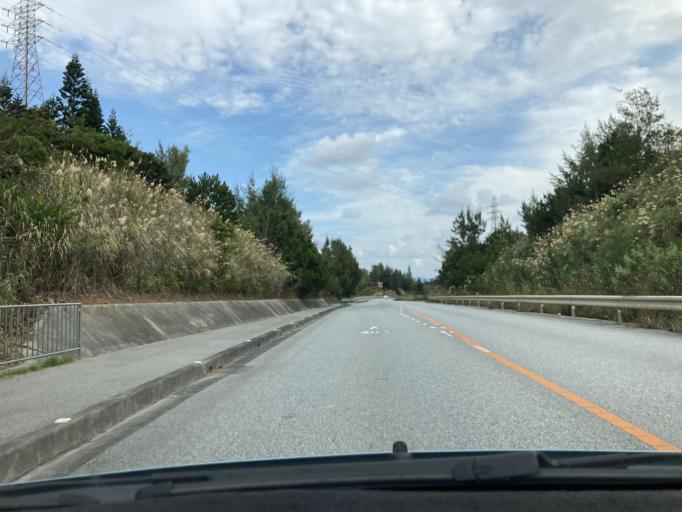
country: JP
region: Okinawa
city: Ishikawa
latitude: 26.5032
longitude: 127.8691
